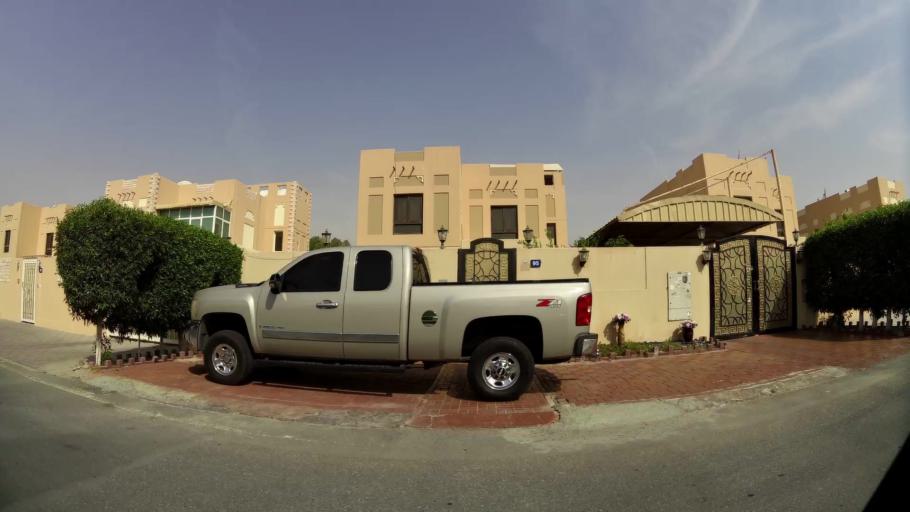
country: AE
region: Ash Shariqah
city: Sharjah
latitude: 25.2636
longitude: 55.4394
